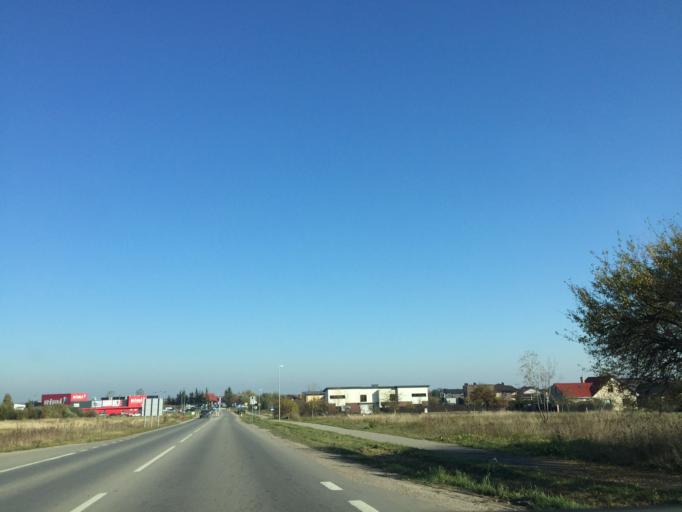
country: LT
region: Klaipedos apskritis
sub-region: Klaipeda
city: Klaipeda
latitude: 55.7341
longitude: 21.1895
